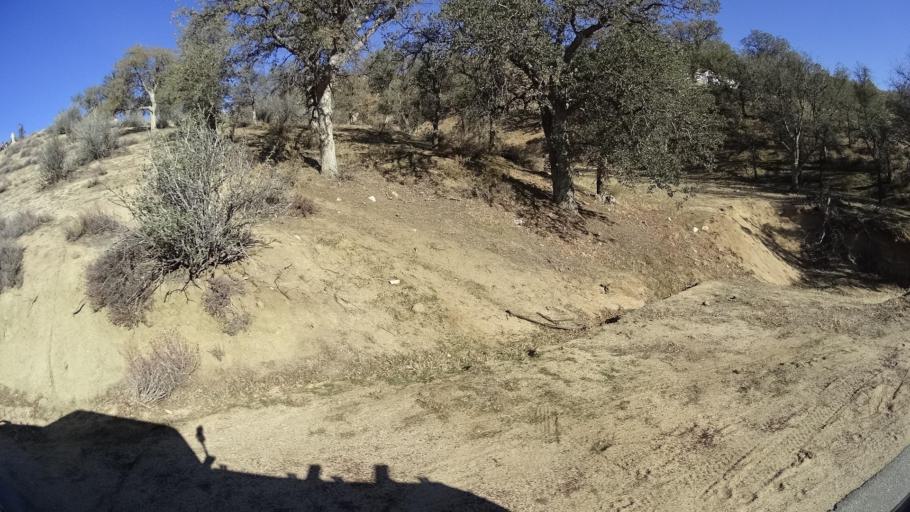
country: US
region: California
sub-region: Kern County
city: Bodfish
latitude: 35.3804
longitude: -118.4034
